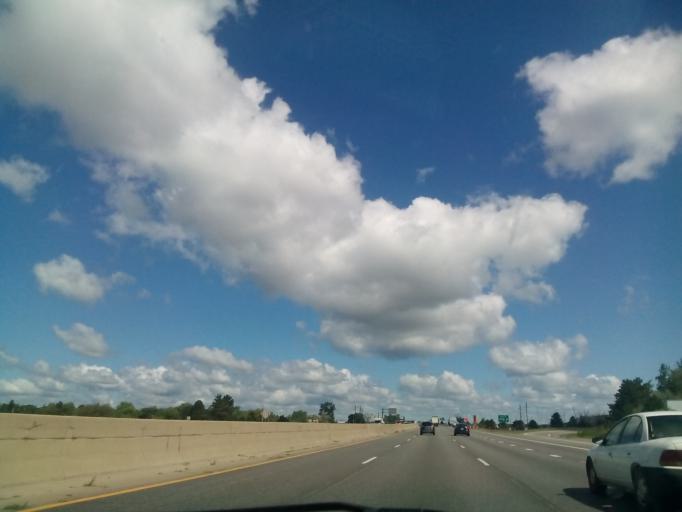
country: US
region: Michigan
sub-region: Genesee County
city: Flint
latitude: 42.9694
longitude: -83.7256
